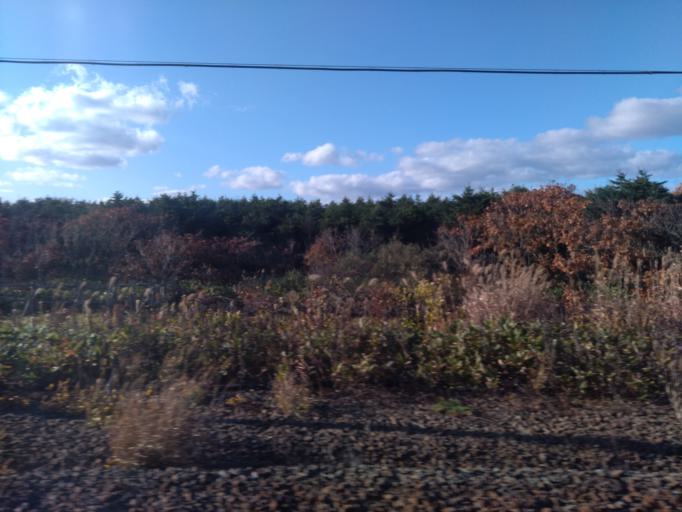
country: JP
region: Hokkaido
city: Niseko Town
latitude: 42.5488
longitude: 140.4156
